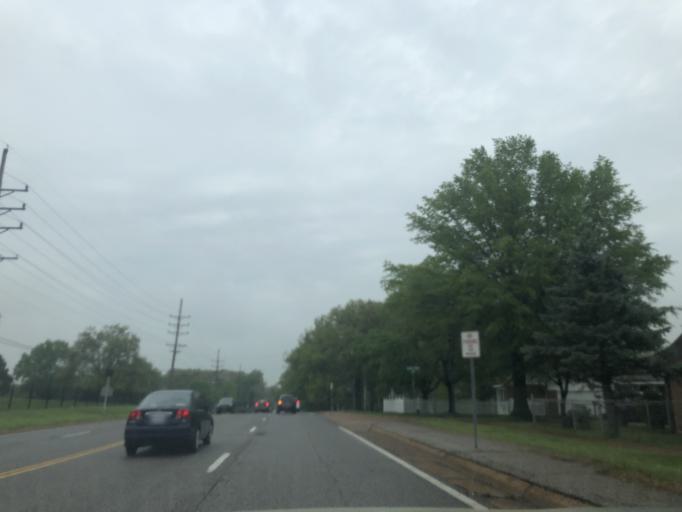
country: US
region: Missouri
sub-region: Saint Louis County
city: Marlborough
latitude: 38.5746
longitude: -90.3194
